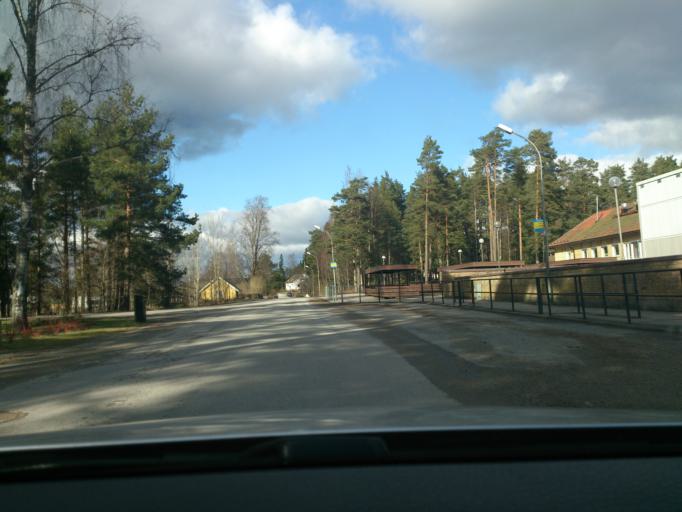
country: SE
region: Kronoberg
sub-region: Alvesta Kommun
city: Moheda
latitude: 56.9982
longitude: 14.5796
